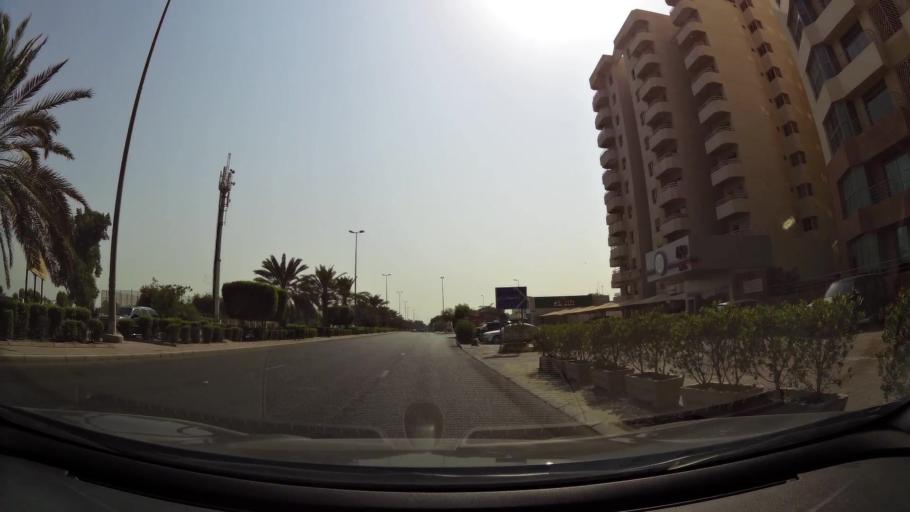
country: KW
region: Al Ahmadi
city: Al Fintas
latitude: 29.1809
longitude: 48.1195
